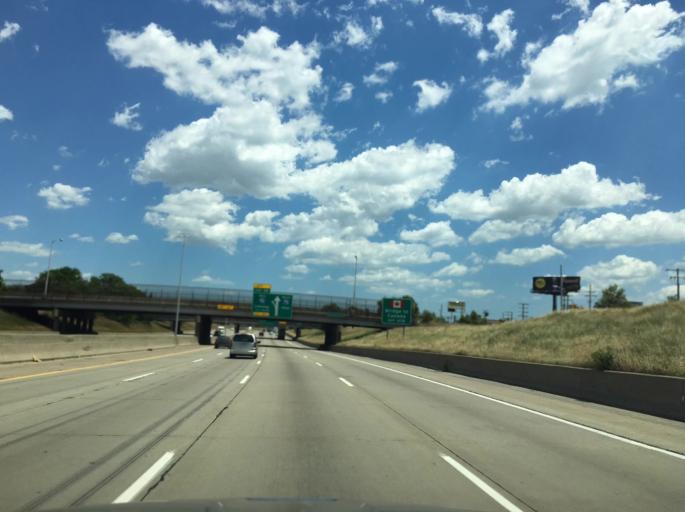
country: US
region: Michigan
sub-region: Wayne County
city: River Rouge
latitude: 42.3070
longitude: -83.1053
